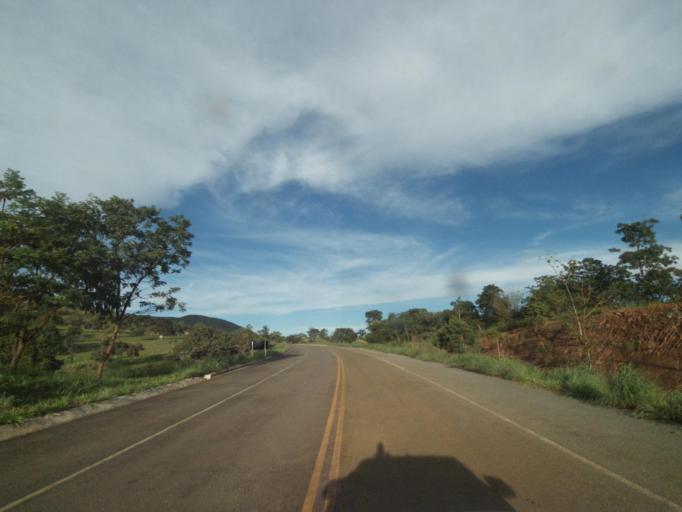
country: BR
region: Goias
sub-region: Jaragua
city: Jaragua
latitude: -15.8430
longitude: -49.3295
